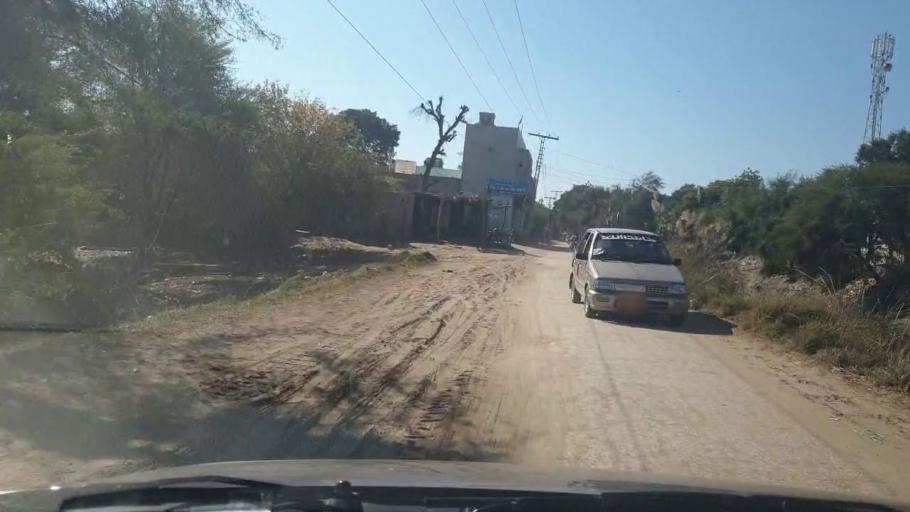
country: PK
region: Sindh
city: Bozdar
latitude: 27.0685
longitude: 68.6186
